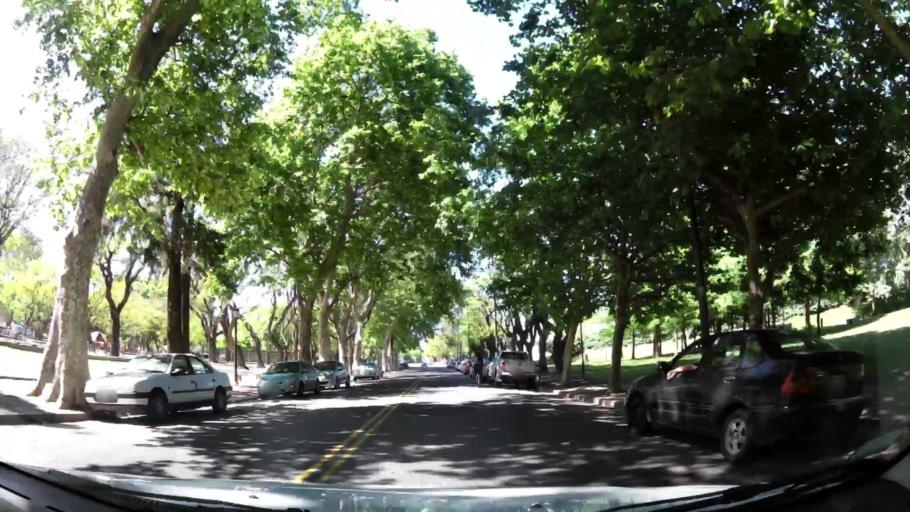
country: AR
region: Buenos Aires F.D.
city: Buenos Aires
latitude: -34.6157
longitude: -58.3583
